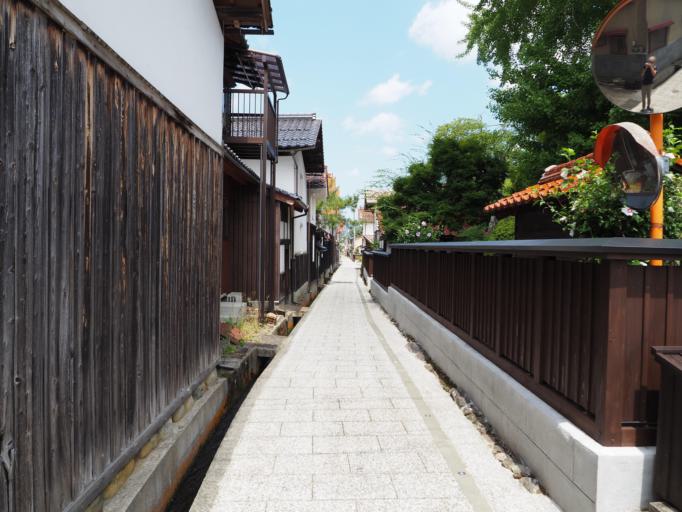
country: JP
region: Tottori
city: Tottori
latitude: 35.3429
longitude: 134.3989
